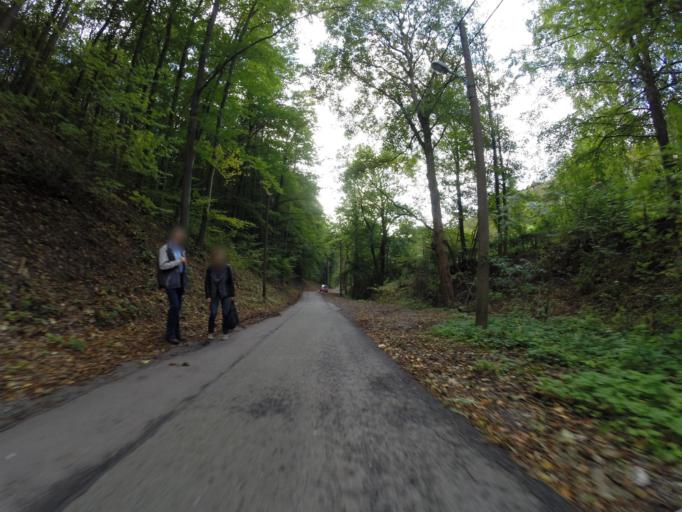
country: DE
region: Thuringia
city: Jena
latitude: 50.9426
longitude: 11.5665
